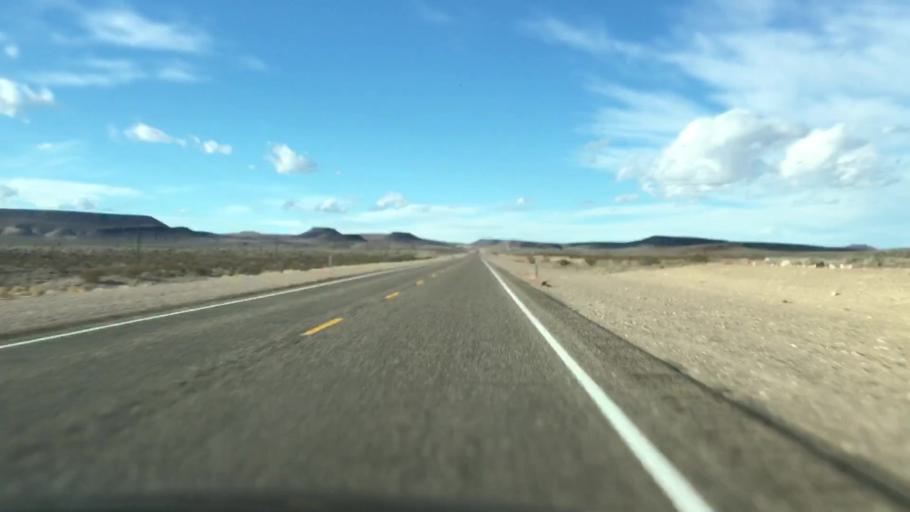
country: US
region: Nevada
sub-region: Esmeralda County
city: Goldfield
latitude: 37.3577
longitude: -117.1130
